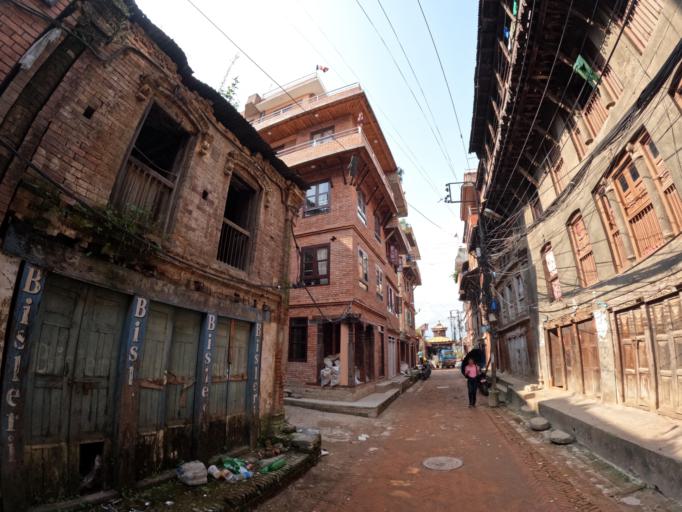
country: NP
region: Central Region
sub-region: Bagmati Zone
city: Bhaktapur
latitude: 27.6740
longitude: 85.4306
